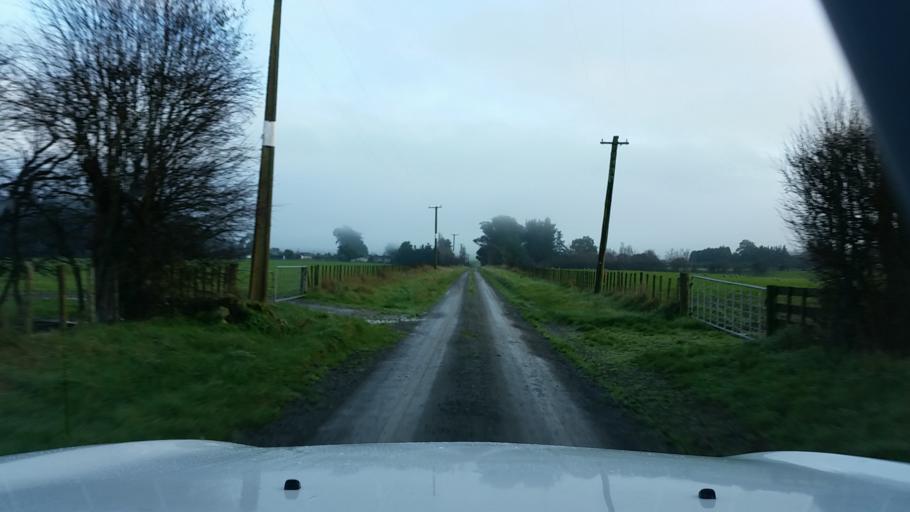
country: NZ
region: Wellington
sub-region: Masterton District
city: Masterton
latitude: -41.0812
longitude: 175.6610
